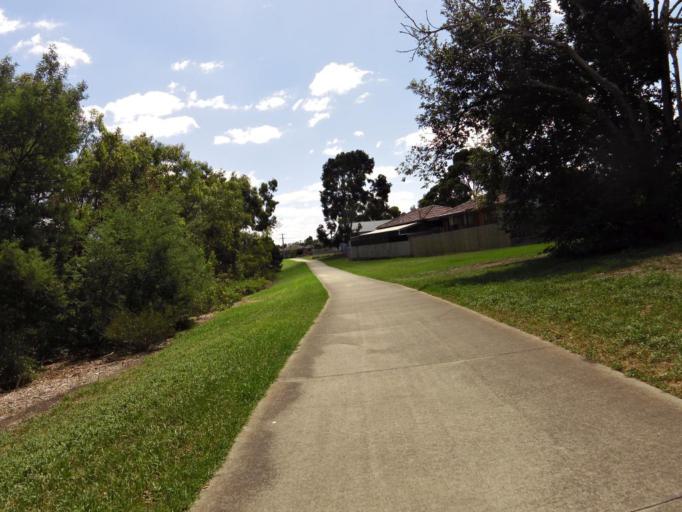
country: AU
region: Victoria
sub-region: Whittlesea
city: Lalor
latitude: -37.6728
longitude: 145.0097
